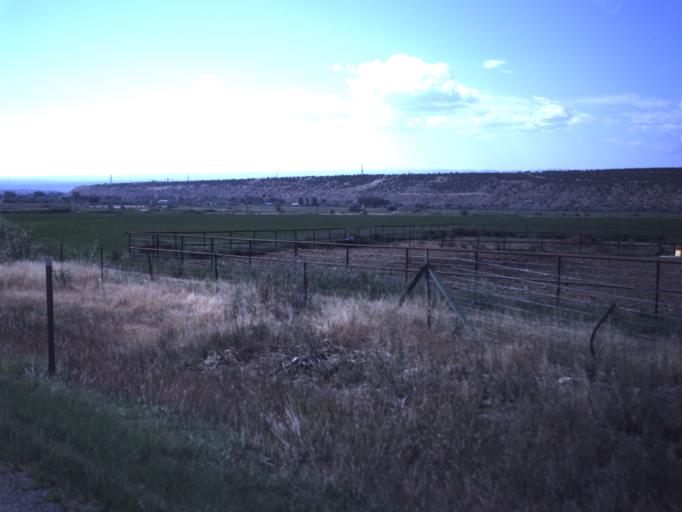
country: US
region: Utah
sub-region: Duchesne County
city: Duchesne
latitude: 40.2691
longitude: -110.4208
